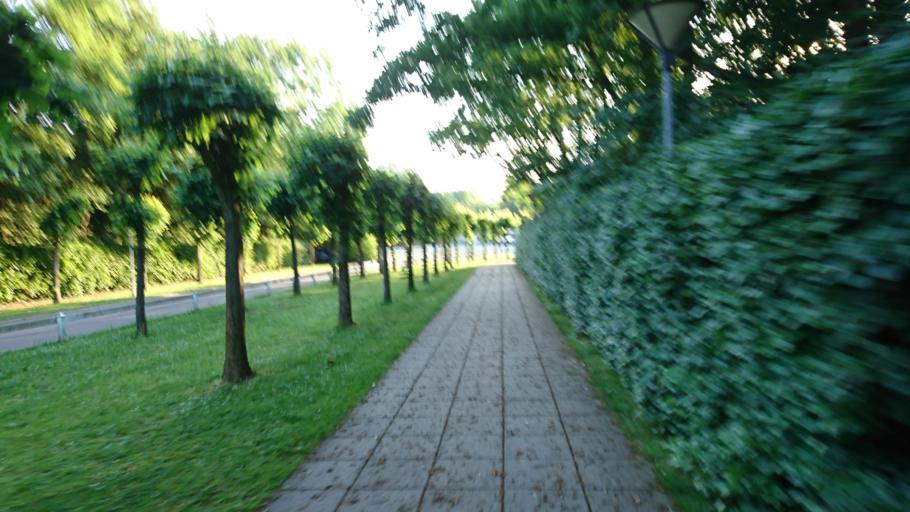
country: DK
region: Capital Region
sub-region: Ballerup Kommune
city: Ballerup
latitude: 55.7205
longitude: 12.3618
